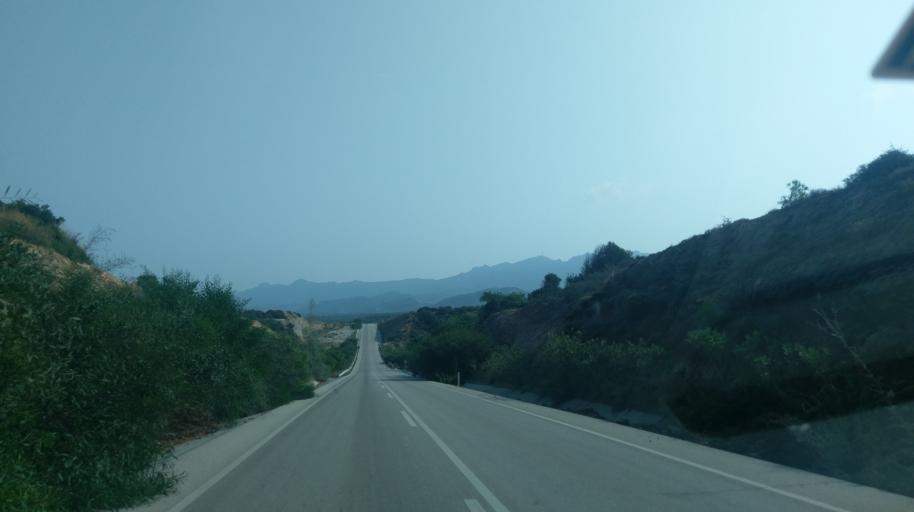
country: CY
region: Ammochostos
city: Trikomo
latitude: 35.4110
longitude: 33.8064
